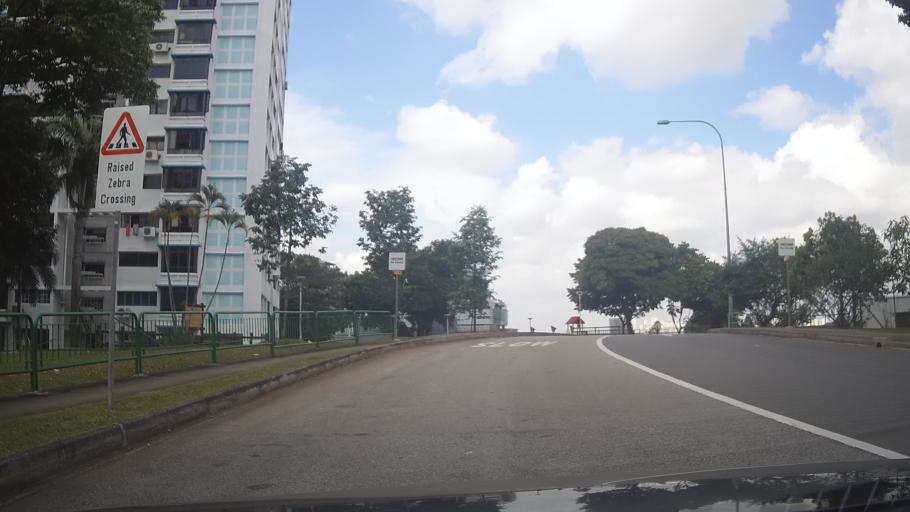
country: MY
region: Johor
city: Johor Bahru
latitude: 1.4458
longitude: 103.7725
